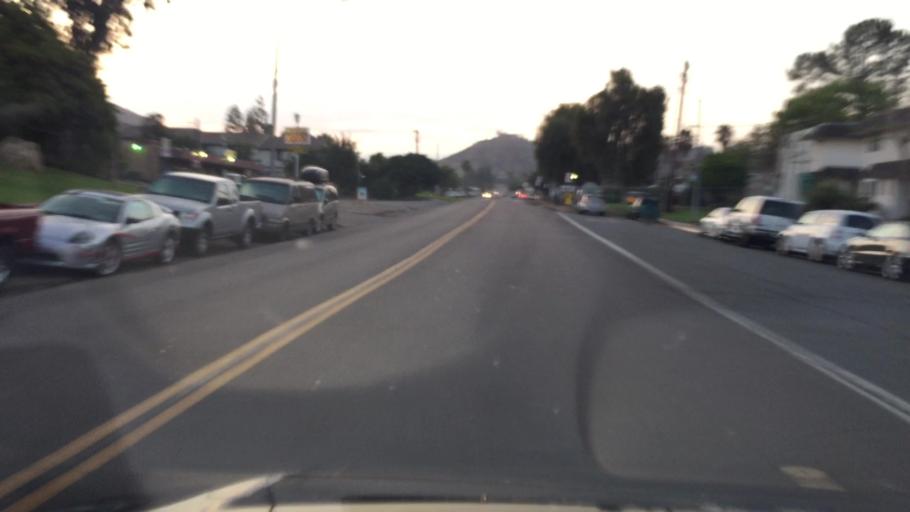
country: US
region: California
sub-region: San Diego County
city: Bostonia
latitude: 32.8191
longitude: -116.9571
